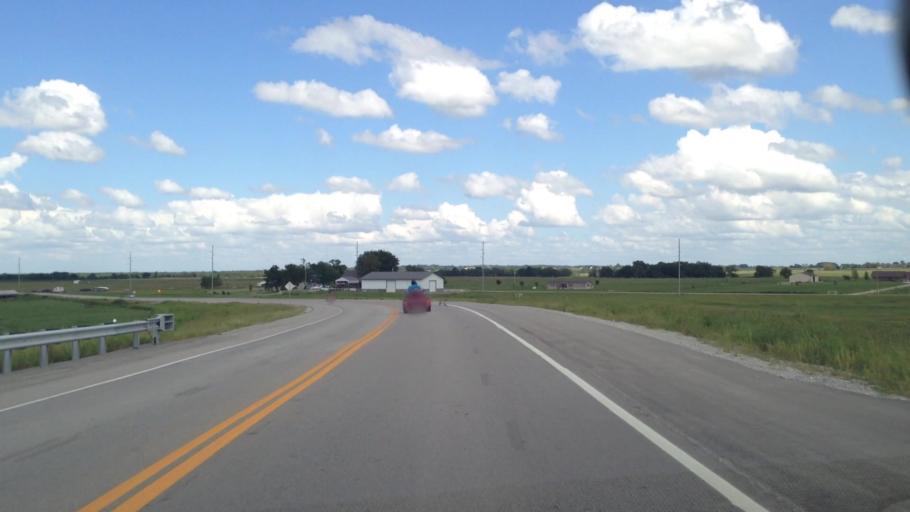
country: US
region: Kansas
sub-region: Labette County
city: Chetopa
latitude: 36.8913
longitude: -95.0936
